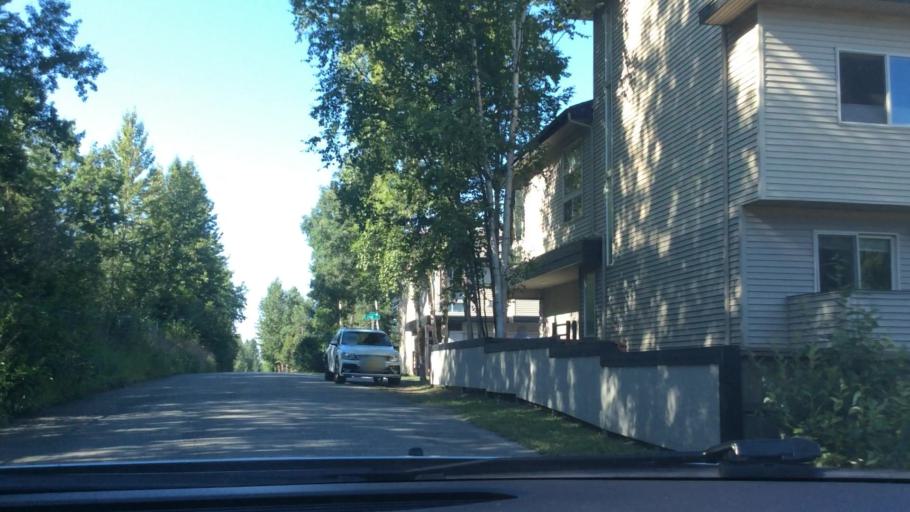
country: US
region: Alaska
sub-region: Anchorage Municipality
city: Anchorage
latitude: 61.1530
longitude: -149.8362
